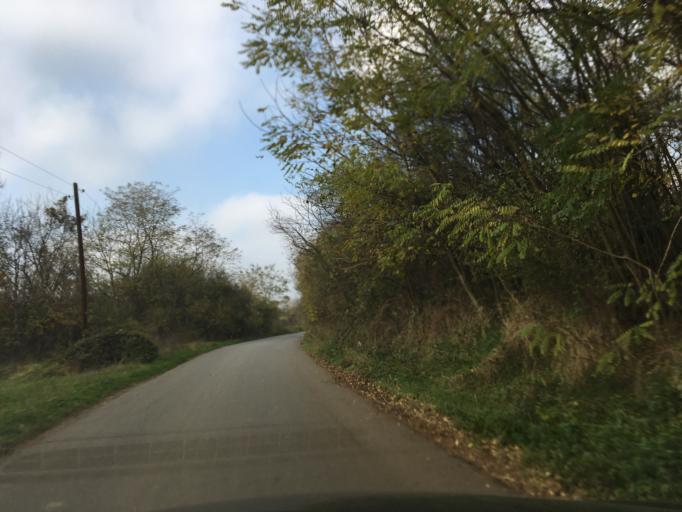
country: RS
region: Central Serbia
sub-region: Belgrade
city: Sopot
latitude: 44.4917
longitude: 20.5883
